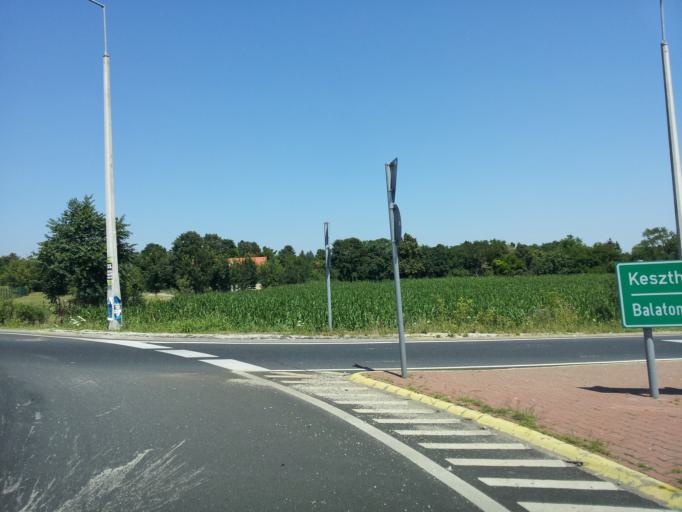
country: HU
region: Veszprem
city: Balatonkenese
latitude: 47.0152
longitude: 18.1681
